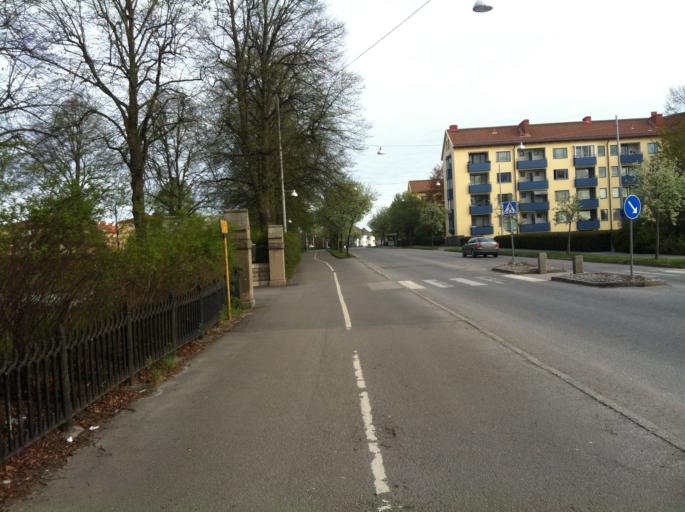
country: SE
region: OEstergoetland
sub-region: Norrkopings Kommun
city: Norrkoping
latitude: 58.5767
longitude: 16.1982
